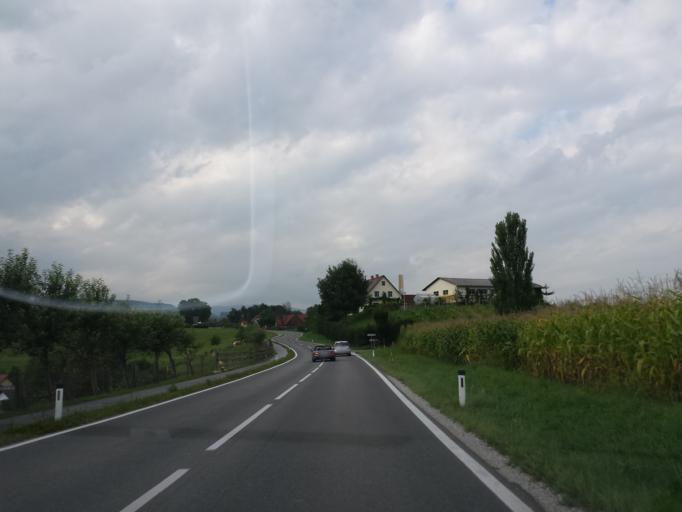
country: AT
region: Styria
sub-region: Politischer Bezirk Deutschlandsberg
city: Rassach
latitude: 46.8637
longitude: 15.2650
